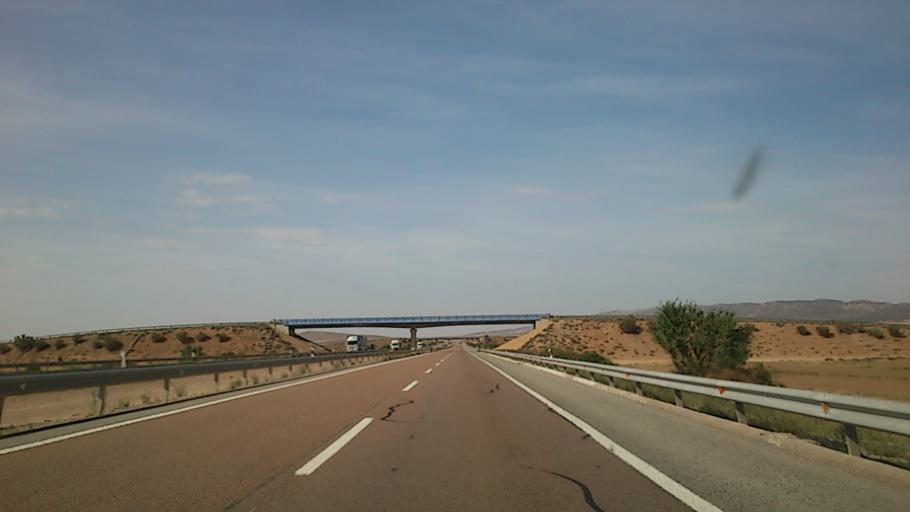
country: ES
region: Aragon
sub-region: Provincia de Teruel
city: Santa Eulalia
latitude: 40.5874
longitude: -1.2848
